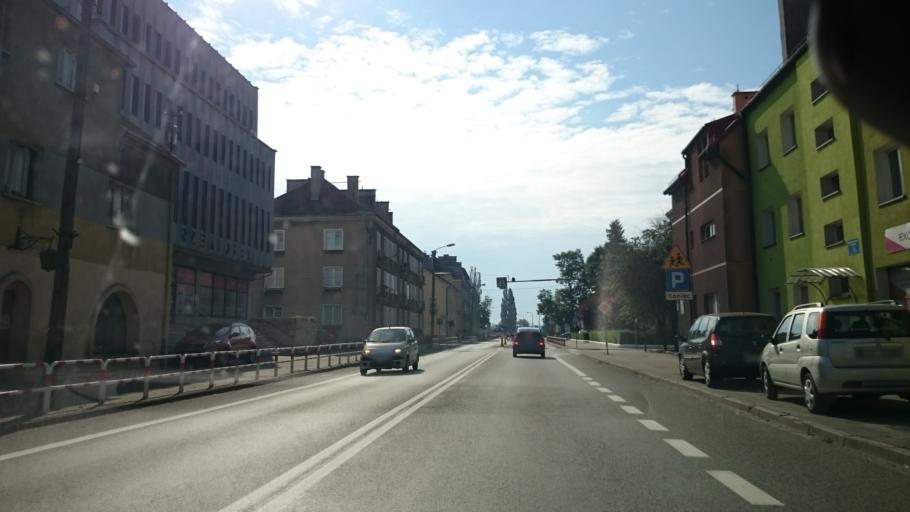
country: PL
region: Opole Voivodeship
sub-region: Powiat strzelecki
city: Strzelce Opolskie
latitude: 50.5085
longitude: 18.3072
